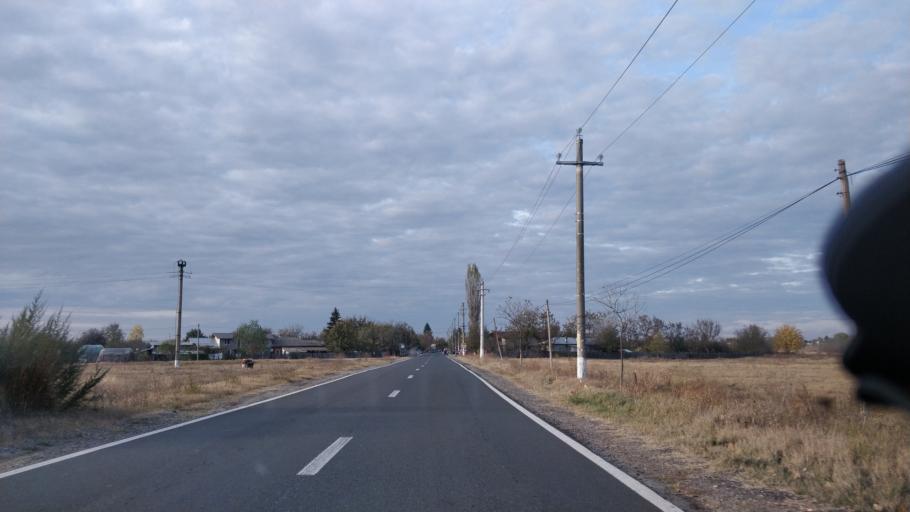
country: RO
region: Giurgiu
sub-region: Comuna Bucsani
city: Bucsani
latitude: 44.3587
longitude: 25.6691
